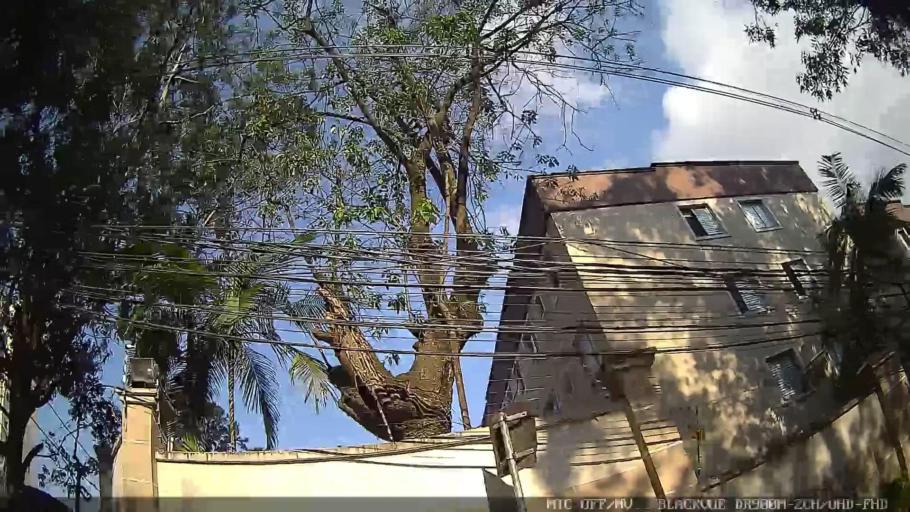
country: BR
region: Sao Paulo
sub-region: Taboao Da Serra
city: Taboao da Serra
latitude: -23.6109
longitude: -46.7259
